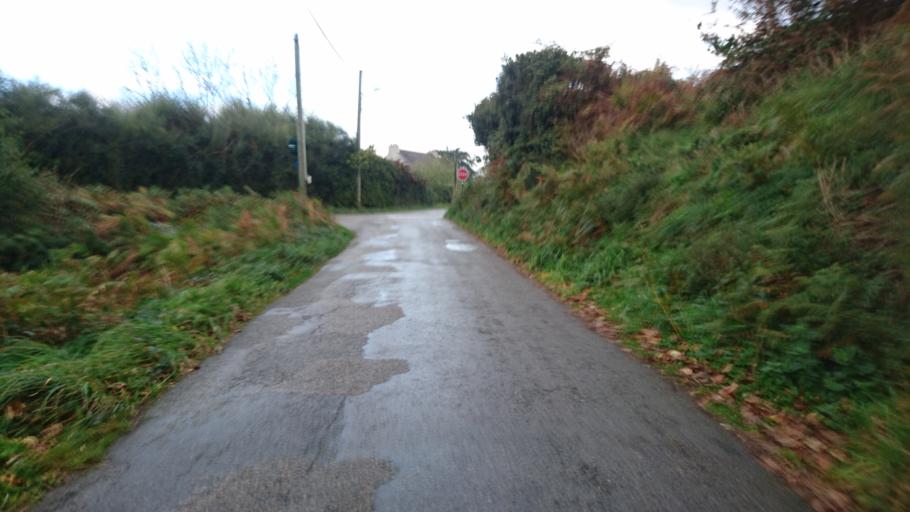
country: FR
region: Brittany
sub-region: Departement du Finistere
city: Lampaul-Plouarzel
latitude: 48.4432
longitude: -4.7693
